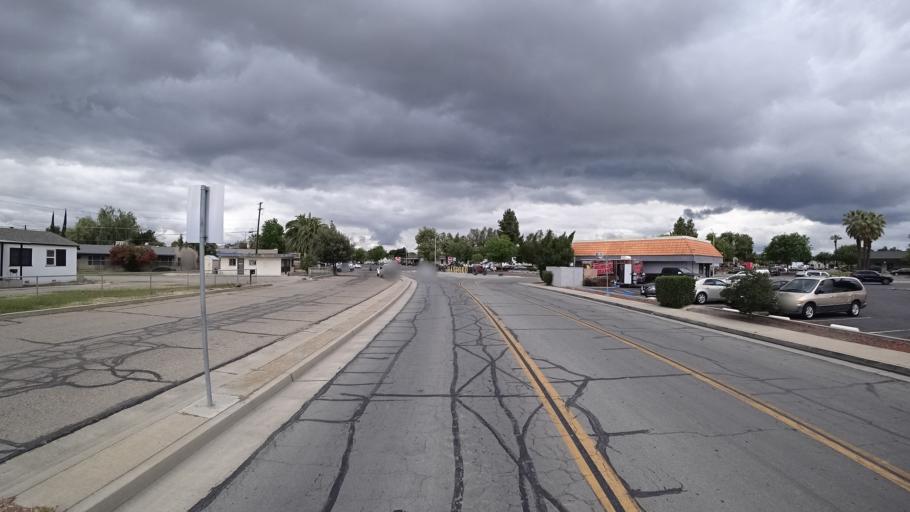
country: US
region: California
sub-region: Kings County
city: Hanford
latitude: 36.3274
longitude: -119.6589
